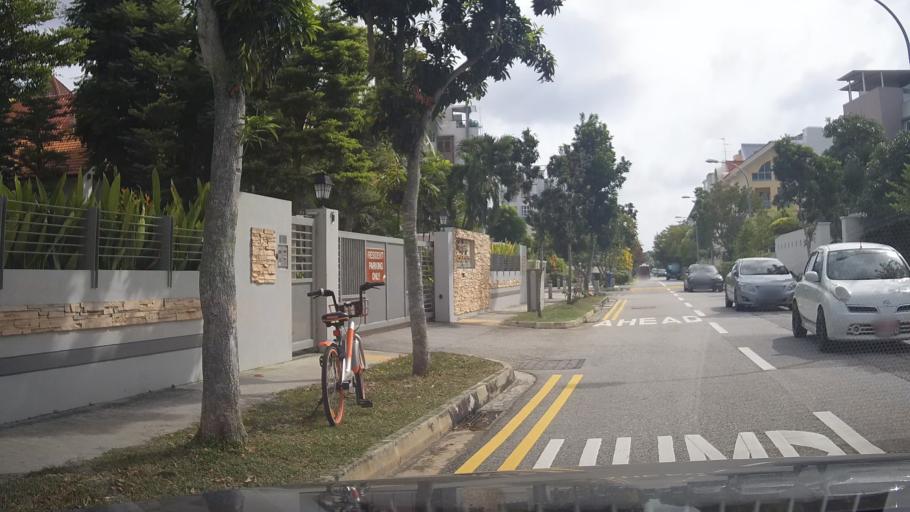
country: SG
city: Singapore
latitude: 1.3122
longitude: 103.9129
